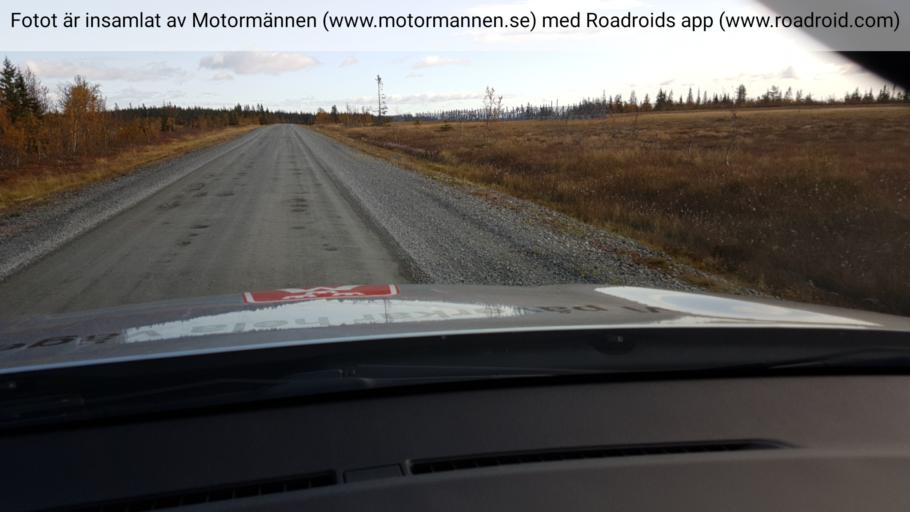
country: SE
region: Vaesterbotten
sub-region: Vilhelmina Kommun
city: Sjoberg
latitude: 64.7595
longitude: 15.8552
